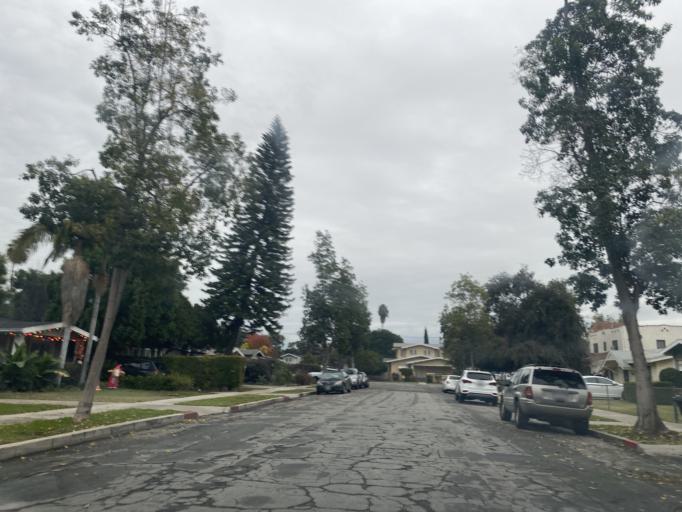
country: US
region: California
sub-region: Orange County
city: Fullerton
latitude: 33.8715
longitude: -117.9164
